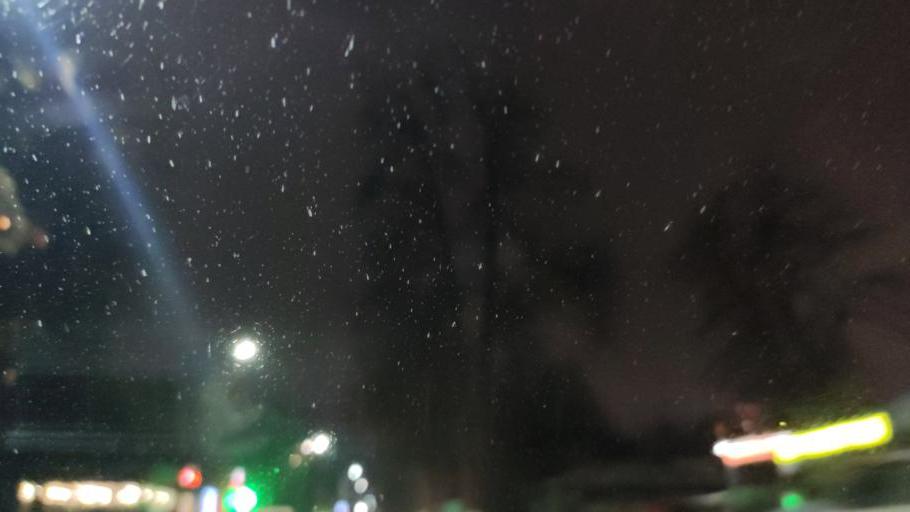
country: RU
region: Moskovskaya
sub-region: Podol'skiy Rayon
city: Podol'sk
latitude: 55.4282
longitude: 37.5430
